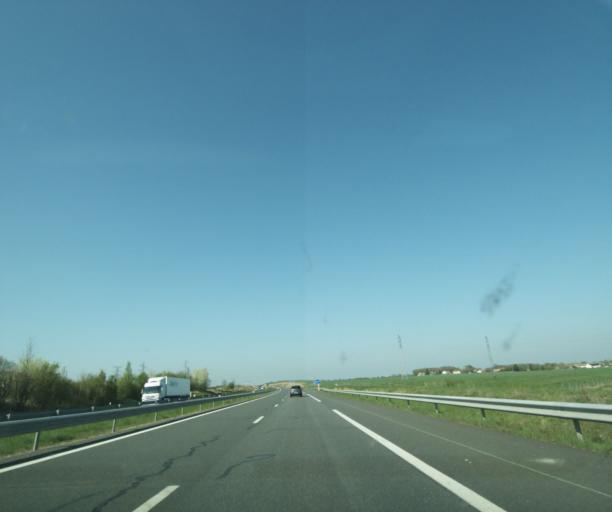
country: FR
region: Centre
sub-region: Departement du Loiret
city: Pannes
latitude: 48.0063
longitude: 2.6801
